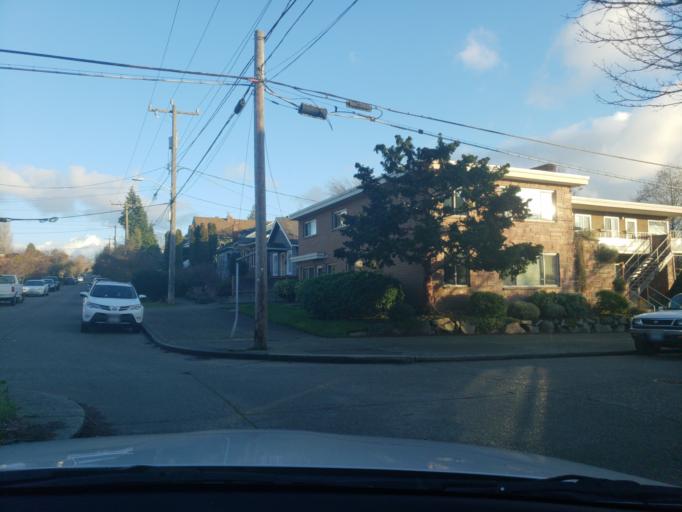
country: US
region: Washington
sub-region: King County
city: Shoreline
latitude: 47.6833
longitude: -122.3634
